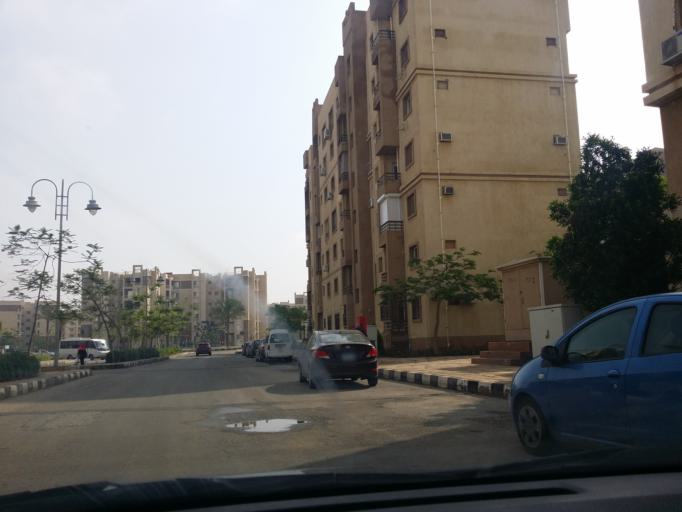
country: EG
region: Muhafazat al Qalyubiyah
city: Al Khankah
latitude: 30.0832
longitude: 31.6457
